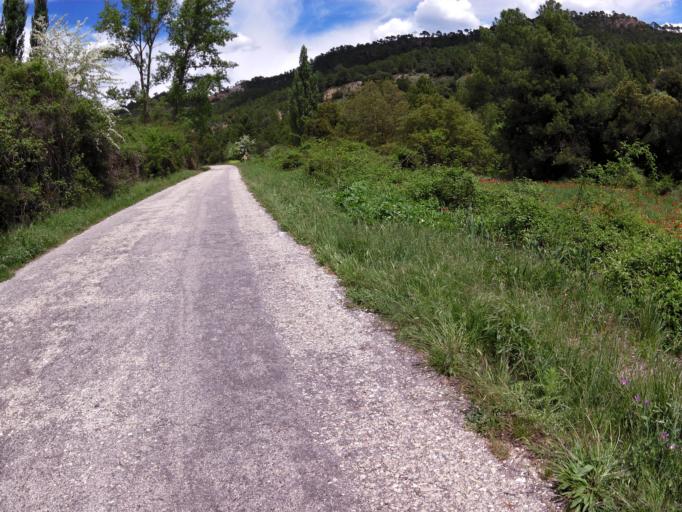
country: ES
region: Castille-La Mancha
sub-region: Provincia de Albacete
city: Paterna del Madera
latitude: 38.5766
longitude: -2.3382
